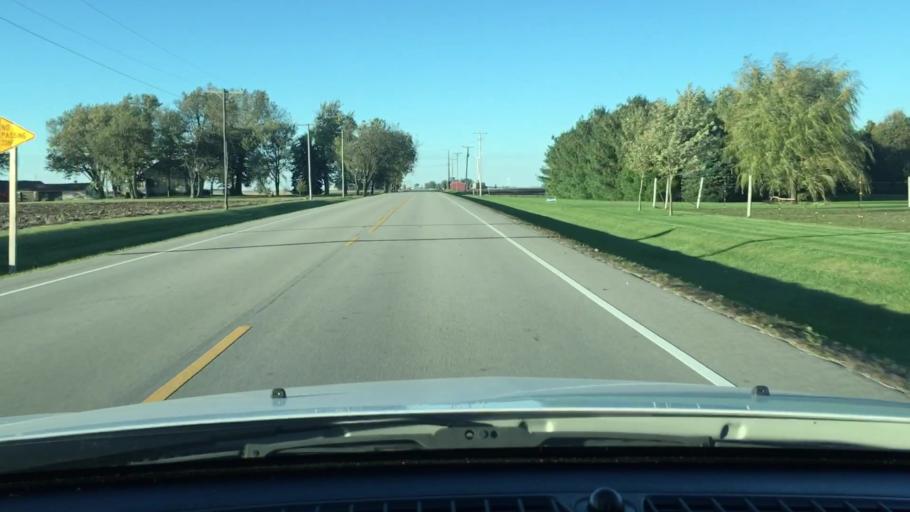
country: US
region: Illinois
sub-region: DeKalb County
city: Malta
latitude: 41.8221
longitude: -88.8864
